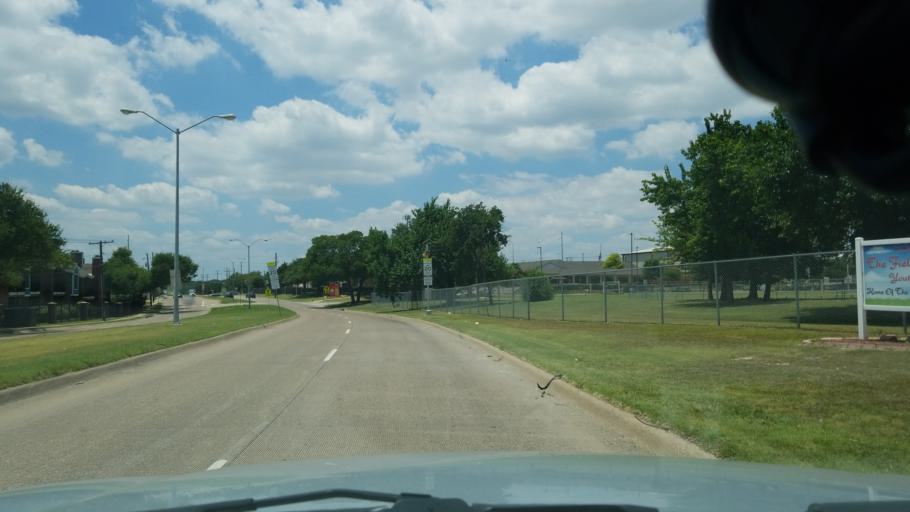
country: US
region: Texas
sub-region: Dallas County
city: Duncanville
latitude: 32.6765
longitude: -96.8795
